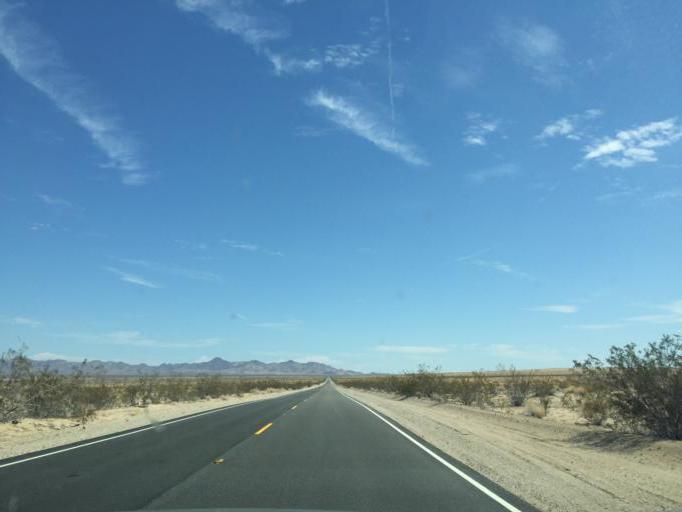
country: US
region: California
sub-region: Riverside County
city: Mesa Verde
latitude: 34.1008
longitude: -114.9949
